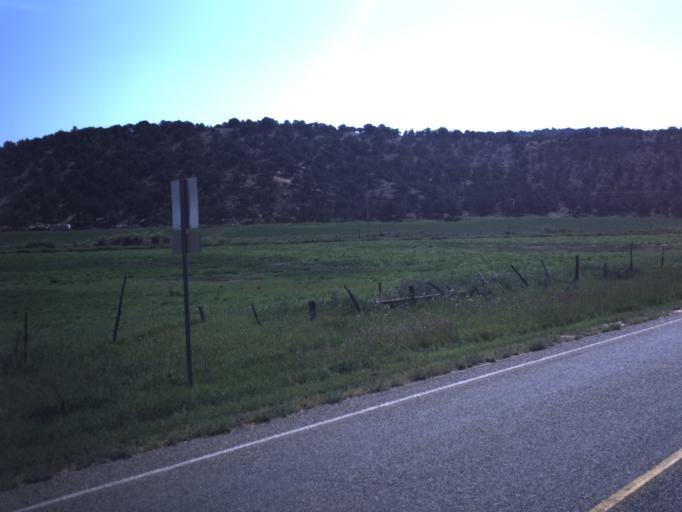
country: US
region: Utah
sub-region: Duchesne County
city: Duchesne
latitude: 40.3344
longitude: -110.6775
